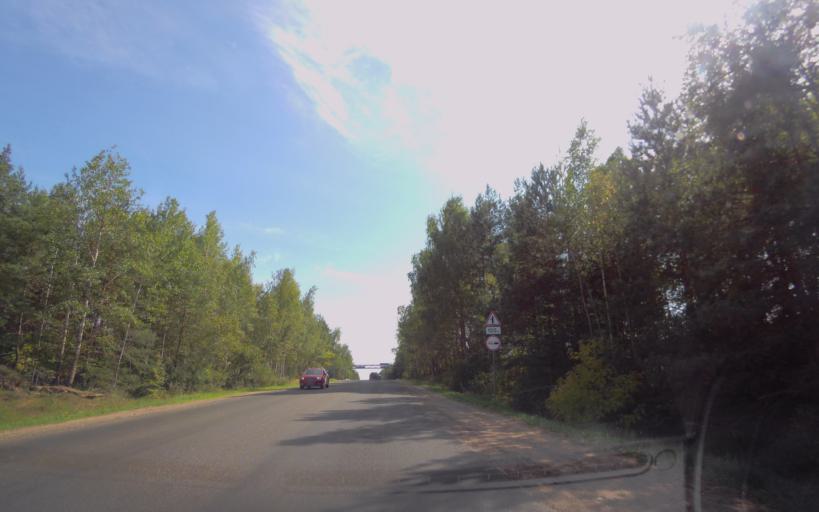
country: BY
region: Minsk
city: Horad Barysaw
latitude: 54.1826
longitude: 28.5684
